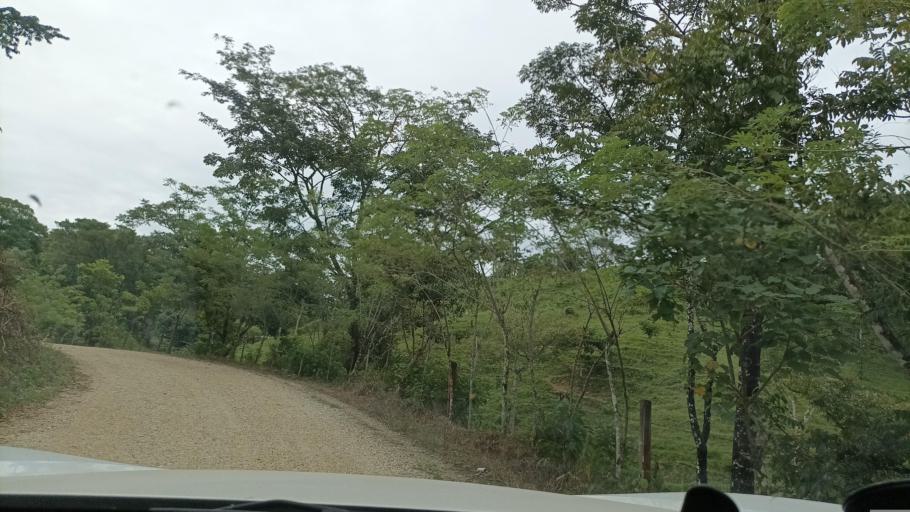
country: MX
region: Veracruz
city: Hidalgotitlan
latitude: 17.5749
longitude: -94.4231
